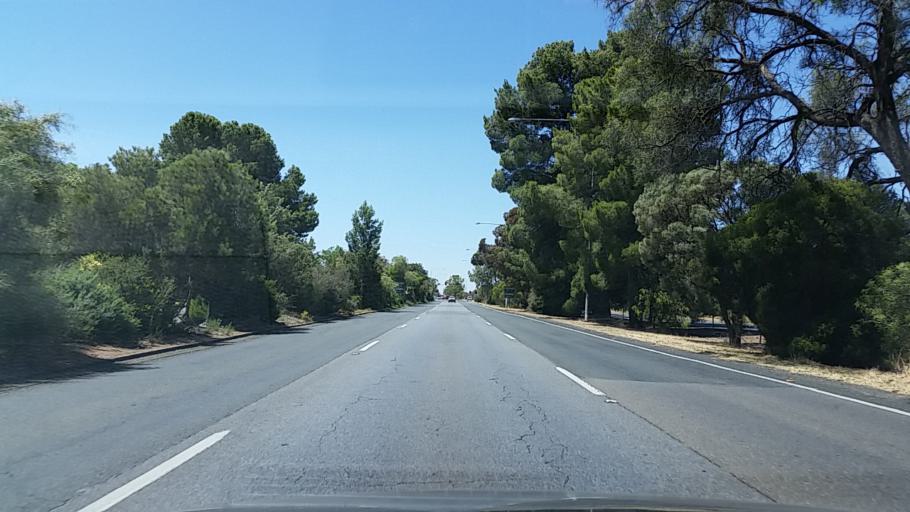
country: AU
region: South Australia
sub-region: Salisbury
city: Elizabeth
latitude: -34.7098
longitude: 138.6768
